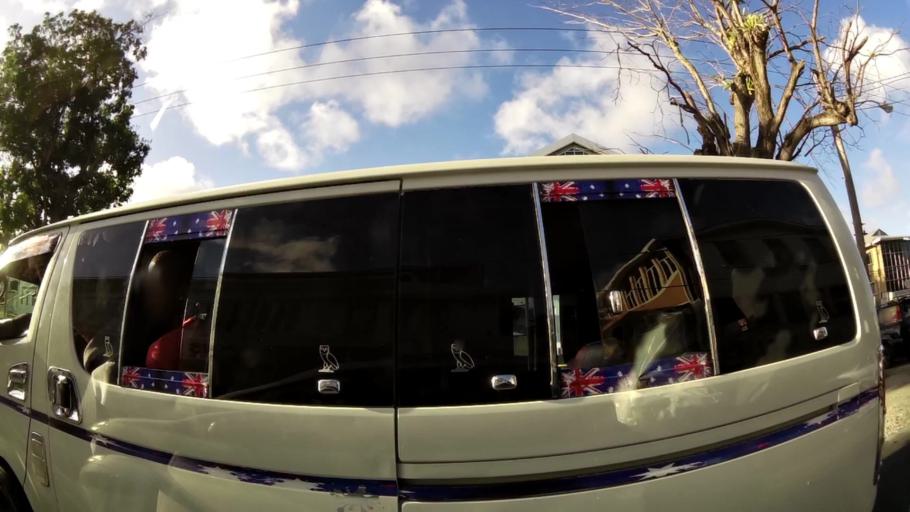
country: GY
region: Demerara-Mahaica
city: Georgetown
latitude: 6.8084
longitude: -58.1611
